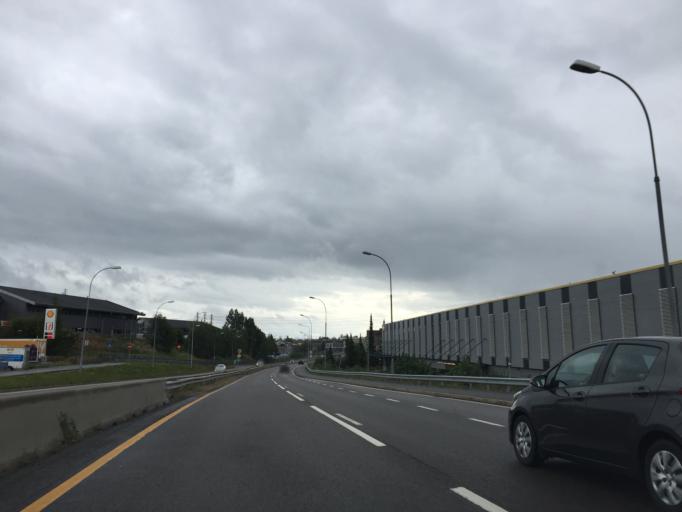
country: NO
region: Akershus
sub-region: Lorenskog
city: Kjenn
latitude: 59.9499
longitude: 10.8846
